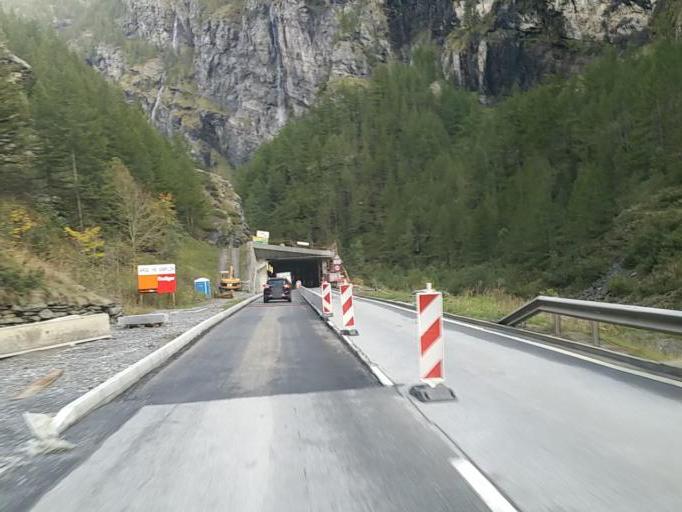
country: IT
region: Piedmont
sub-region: Provincia Verbano-Cusio-Ossola
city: Antronapiana
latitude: 46.1859
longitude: 8.0847
